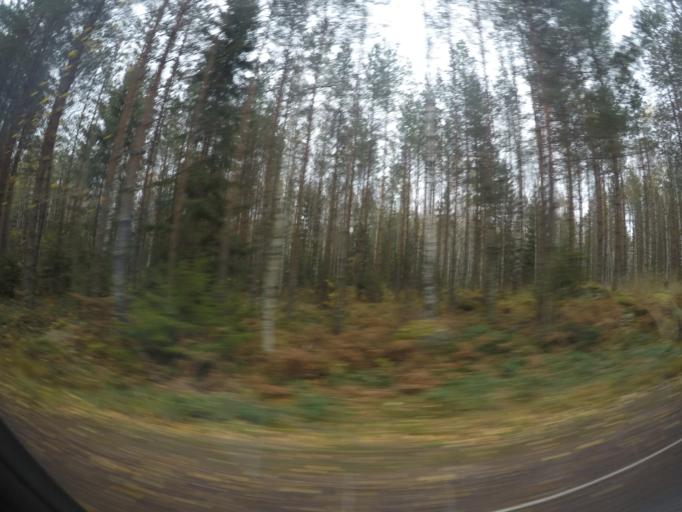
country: SE
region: Vaestmanland
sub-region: Surahammars Kommun
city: Surahammar
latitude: 59.6582
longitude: 16.0779
